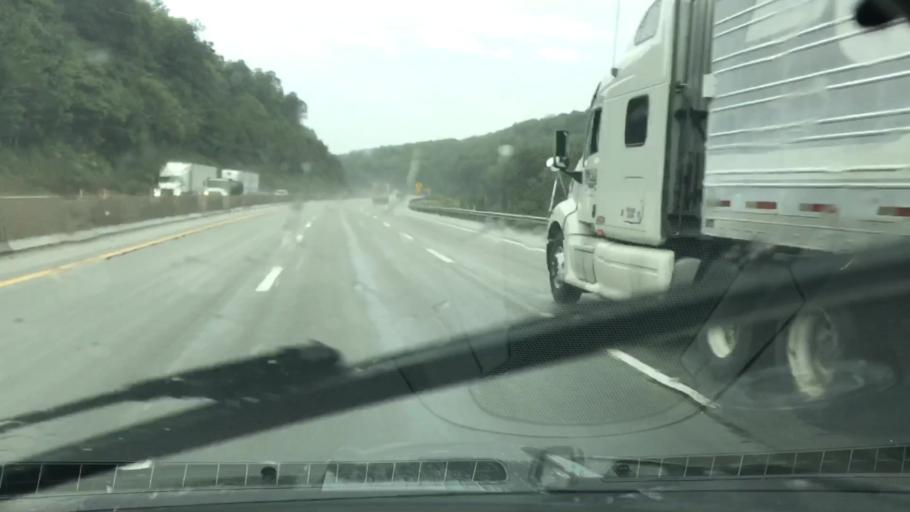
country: US
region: Pennsylvania
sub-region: Fayette County
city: Bear Rocks
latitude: 40.1544
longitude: -79.4328
